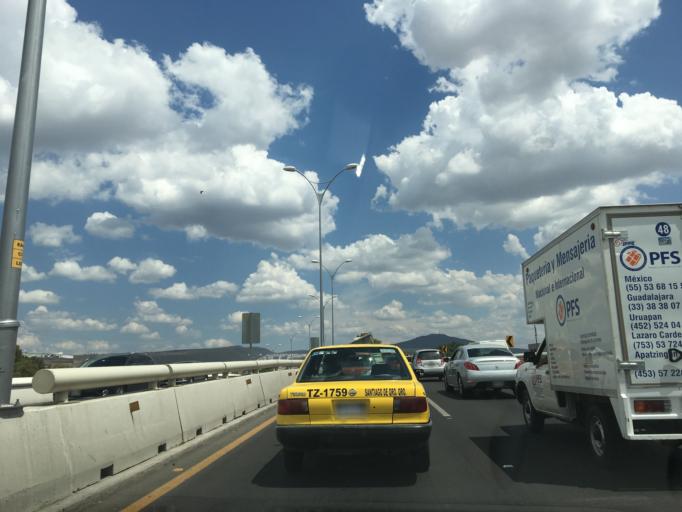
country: MX
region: Queretaro
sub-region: Queretaro
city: Santiago de Queretaro
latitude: 20.6011
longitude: -100.3762
